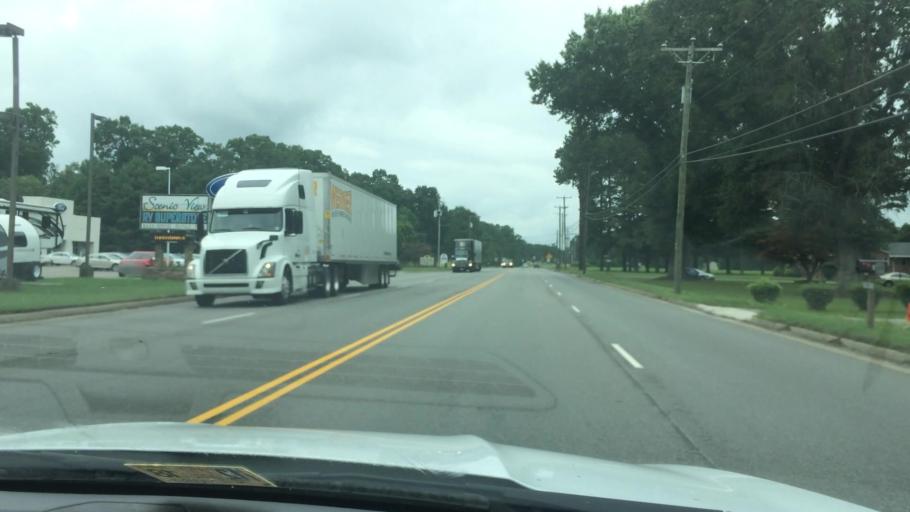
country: US
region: Virginia
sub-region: King William County
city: West Point
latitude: 37.5214
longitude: -76.8295
